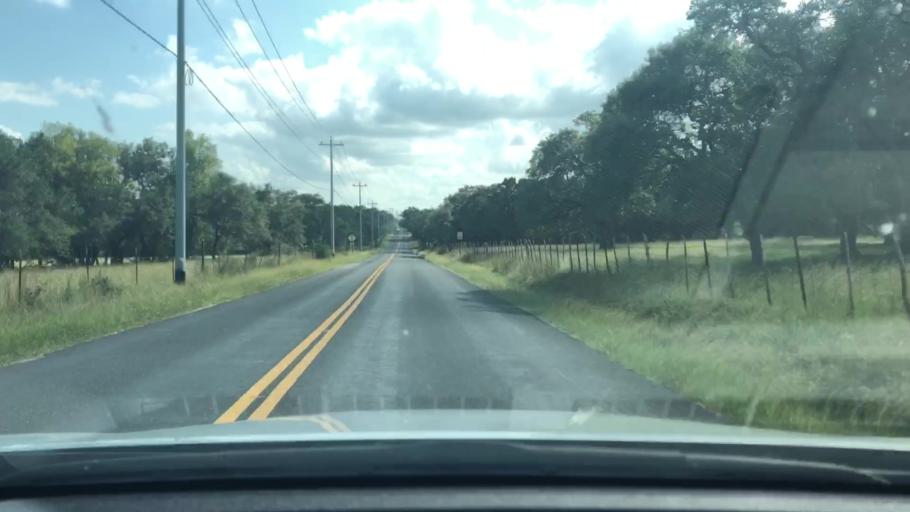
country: US
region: Texas
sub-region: Bexar County
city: Fair Oaks Ranch
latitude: 29.7847
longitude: -98.6268
